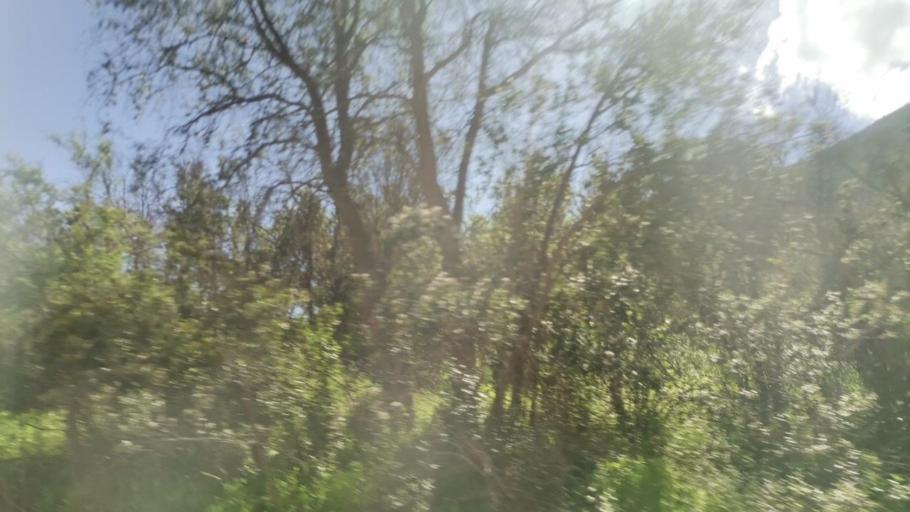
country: CL
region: Valparaiso
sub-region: Provincia de Marga Marga
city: Limache
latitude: -33.1976
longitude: -71.2709
